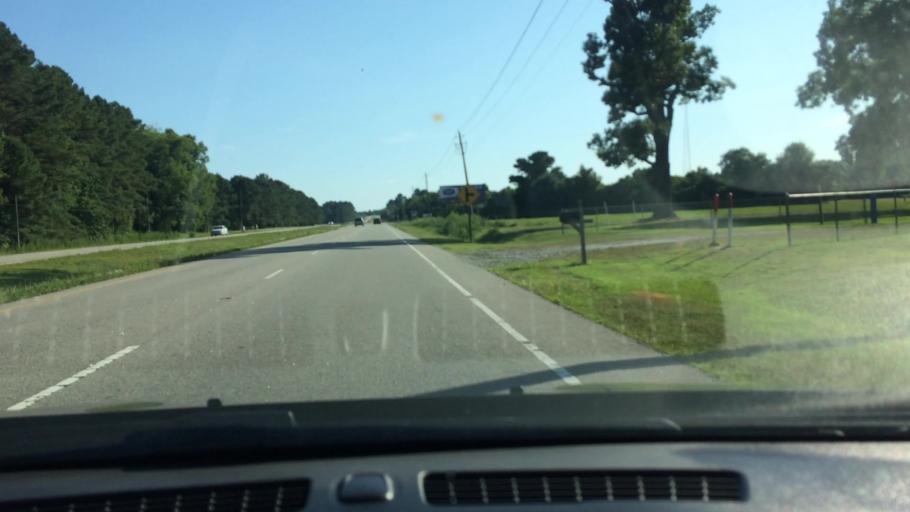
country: US
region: North Carolina
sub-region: Pitt County
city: Grifton
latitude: 35.3405
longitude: -77.4785
